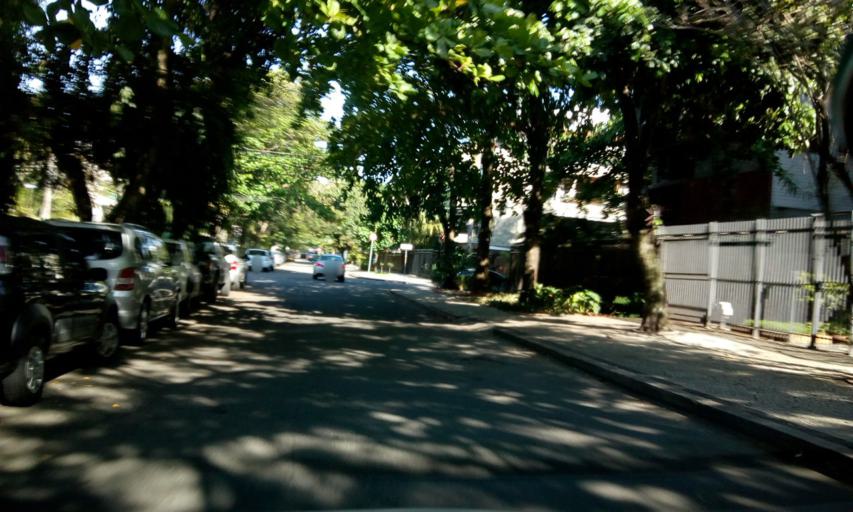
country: BR
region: Rio de Janeiro
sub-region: Rio De Janeiro
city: Rio de Janeiro
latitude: -23.0099
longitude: -43.3111
